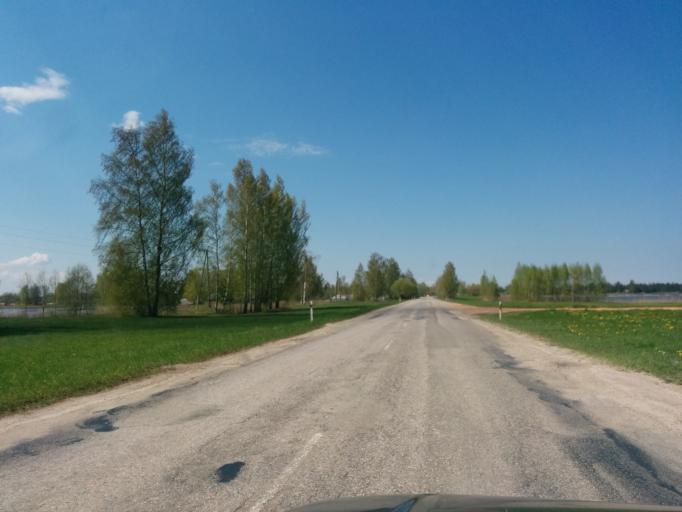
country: LV
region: Ozolnieku
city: Ozolnieki
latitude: 56.6453
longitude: 23.8319
